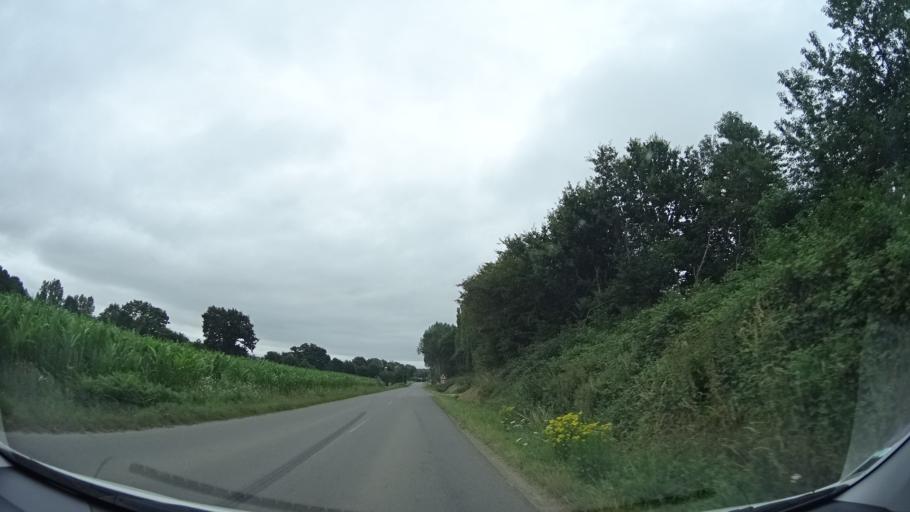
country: FR
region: Brittany
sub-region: Departement d'Ille-et-Vilaine
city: Saint-Domineuc
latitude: 48.3763
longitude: -1.8442
